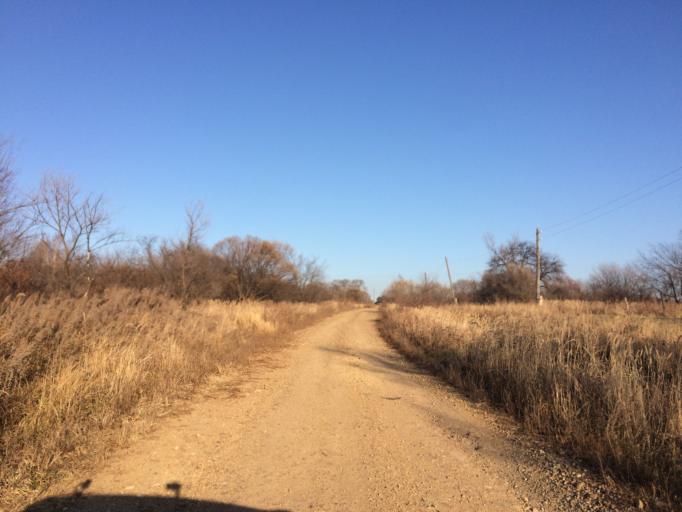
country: RU
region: Primorskiy
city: Ivanovka
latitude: 43.9546
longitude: 132.4643
